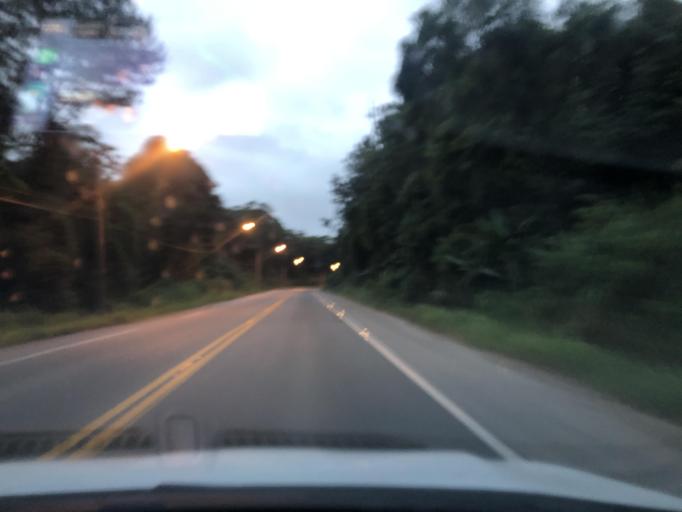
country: BR
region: Santa Catarina
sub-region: Pomerode
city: Pomerode
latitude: -26.7292
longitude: -49.0645
